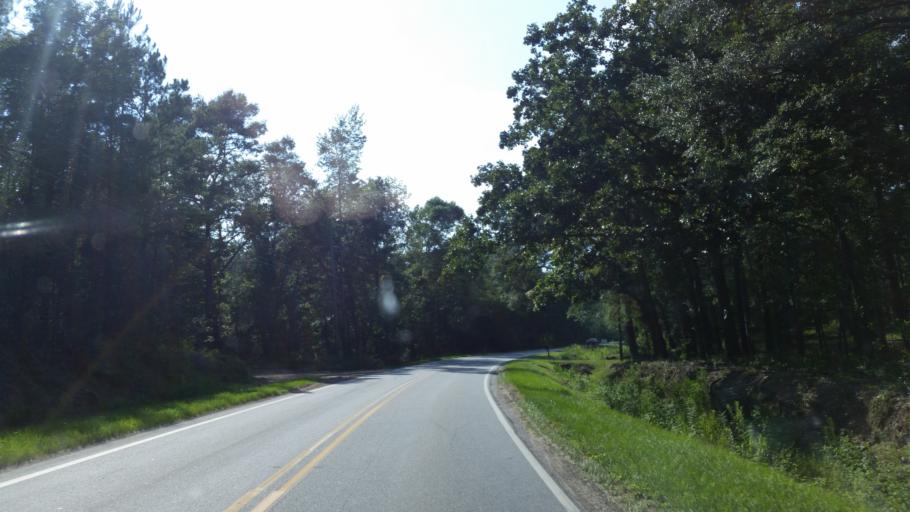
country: US
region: Georgia
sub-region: Lowndes County
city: Remerton
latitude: 30.8942
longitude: -83.3688
